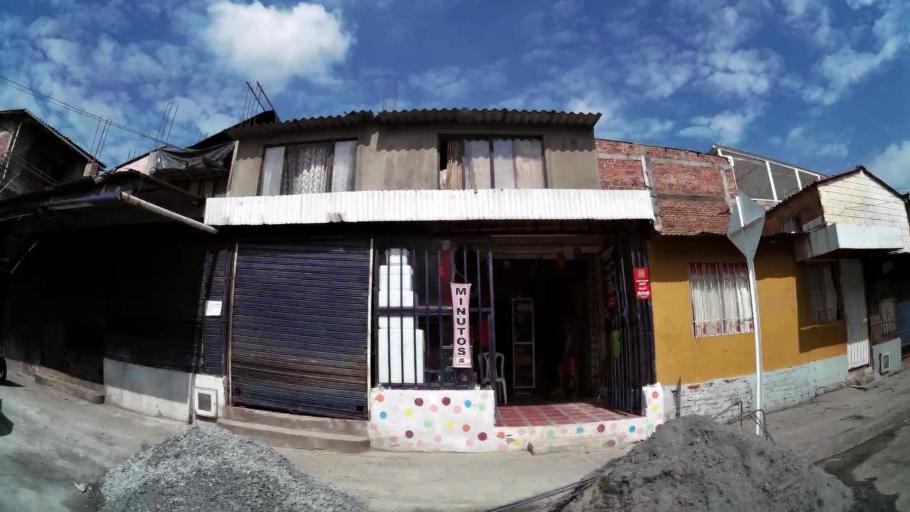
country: CO
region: Valle del Cauca
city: Cali
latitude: 3.4938
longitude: -76.4913
